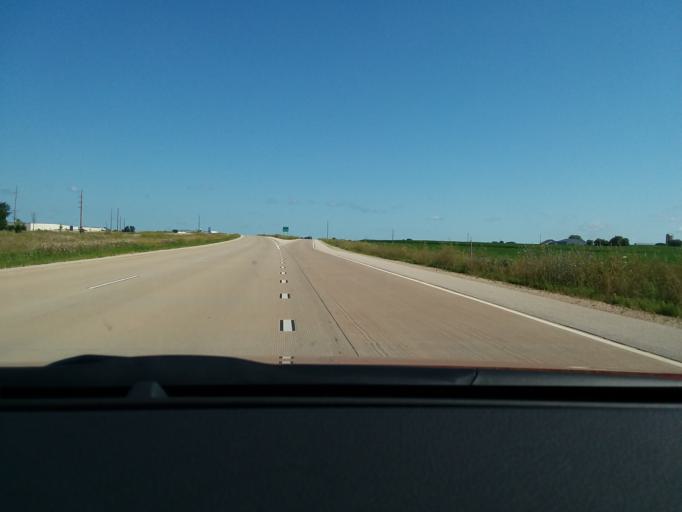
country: US
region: Wisconsin
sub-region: Dane County
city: De Forest
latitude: 43.2463
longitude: -89.3227
